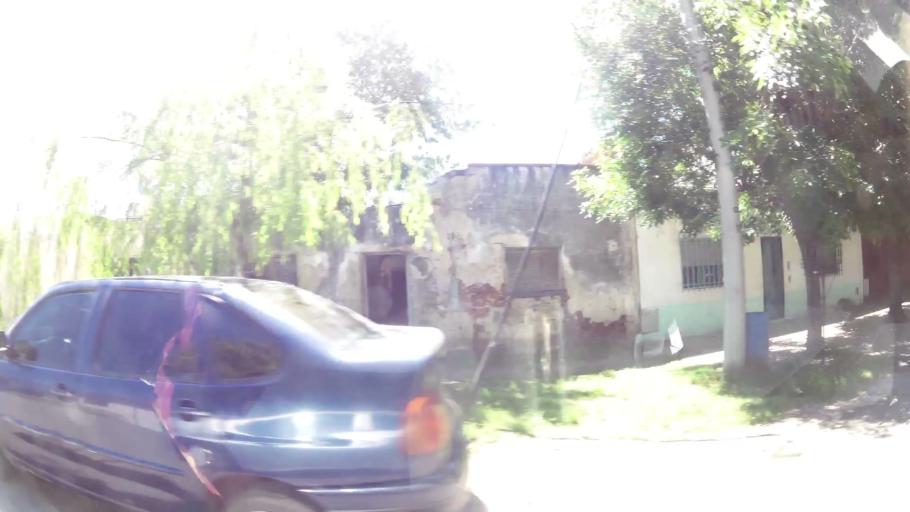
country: AR
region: Santa Fe
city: Perez
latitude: -32.9549
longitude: -60.7166
